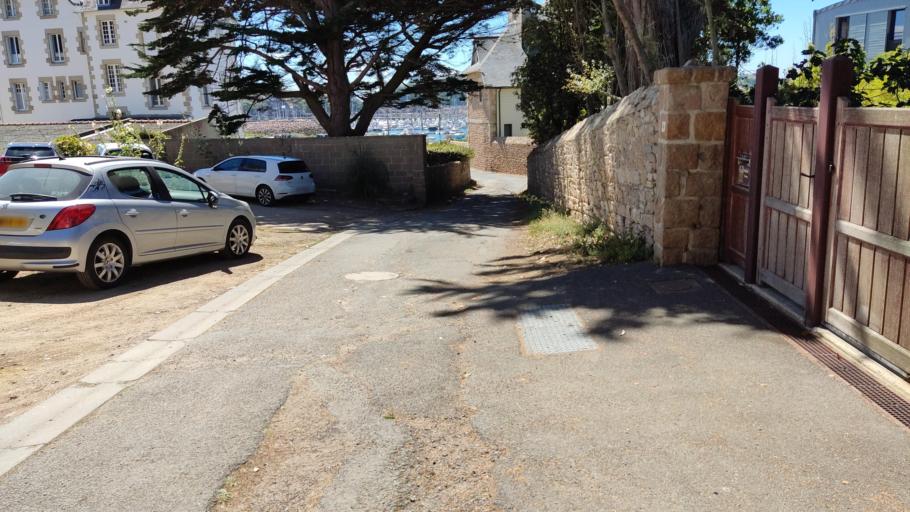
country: FR
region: Brittany
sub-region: Departement des Cotes-d'Armor
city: Trebeurden
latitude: 48.7729
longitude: -3.5831
